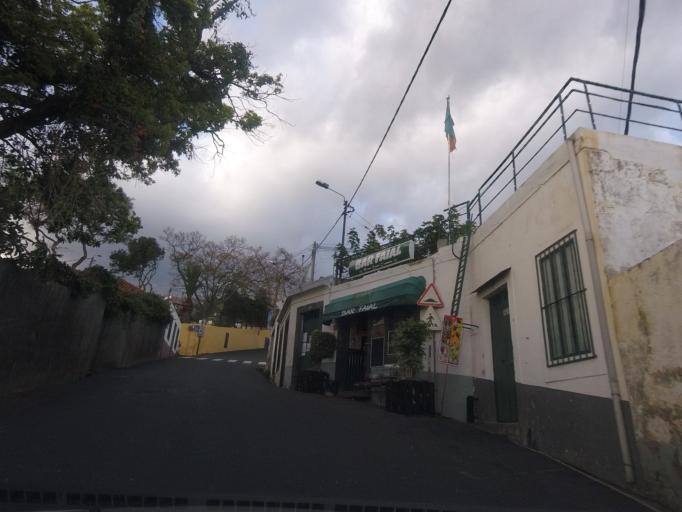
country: PT
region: Madeira
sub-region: Funchal
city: Nossa Senhora do Monte
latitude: 32.6530
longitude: -16.8902
